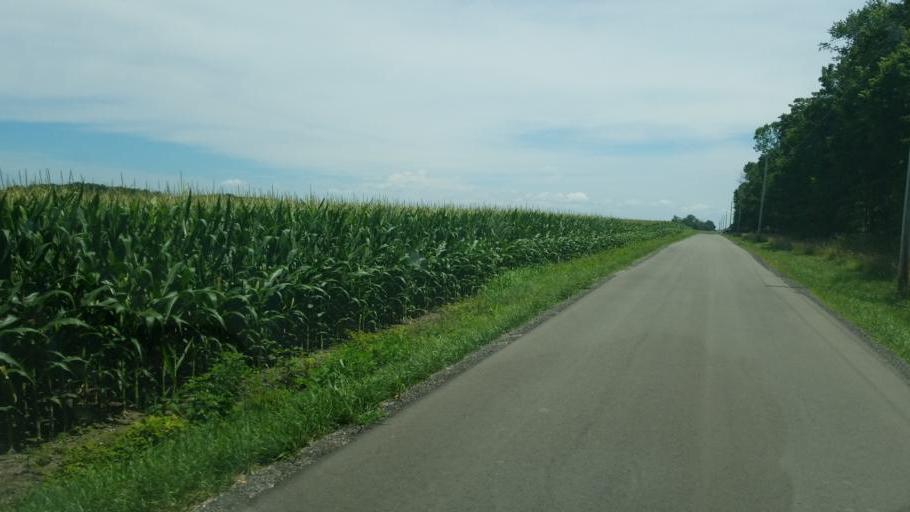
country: US
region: Ohio
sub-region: Crawford County
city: Crestline
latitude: 40.8720
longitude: -82.7646
